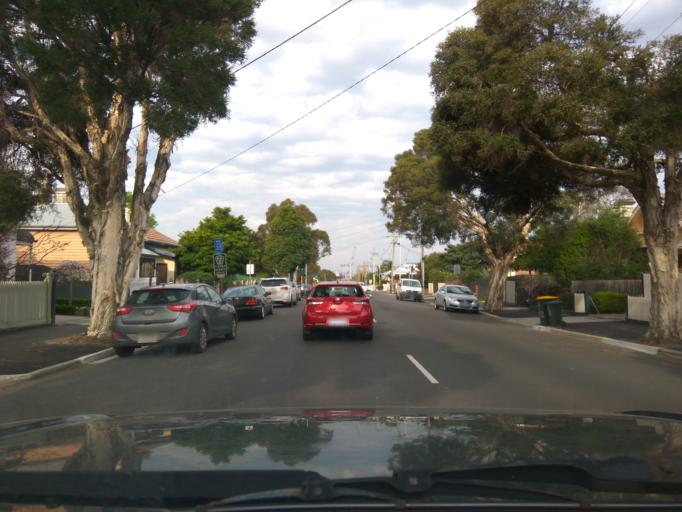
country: AU
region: Victoria
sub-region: Hobsons Bay
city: Newport
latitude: -37.8450
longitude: 144.8912
